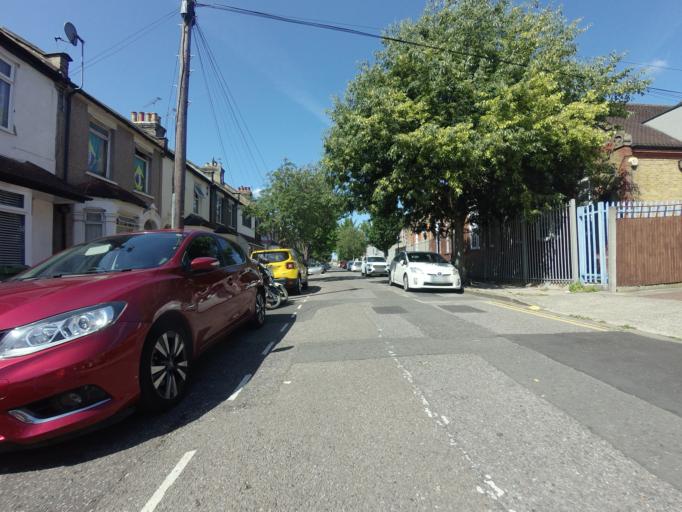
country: GB
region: England
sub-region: Greater London
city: Poplar
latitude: 51.5221
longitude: 0.0095
